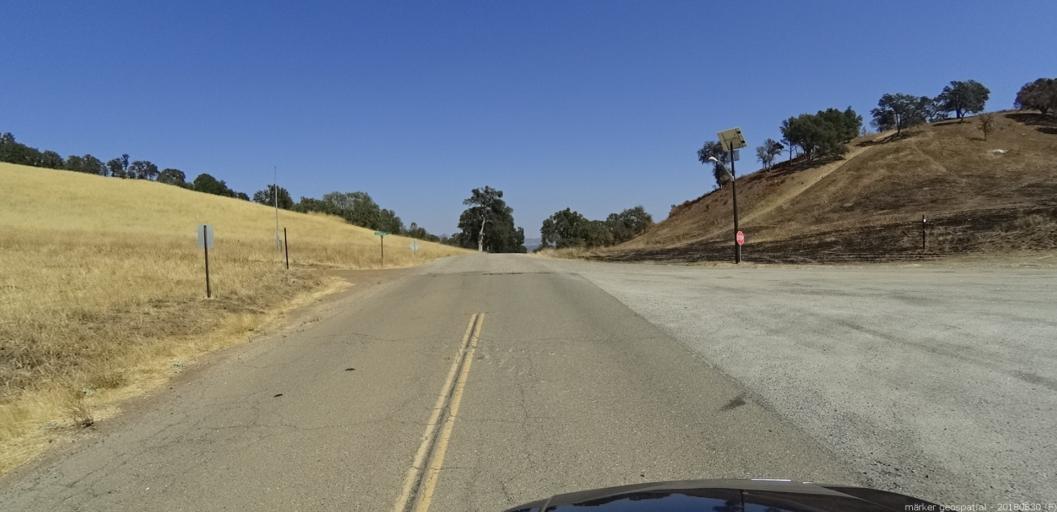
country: US
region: California
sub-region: Monterey County
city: King City
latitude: 35.9704
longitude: -121.2697
